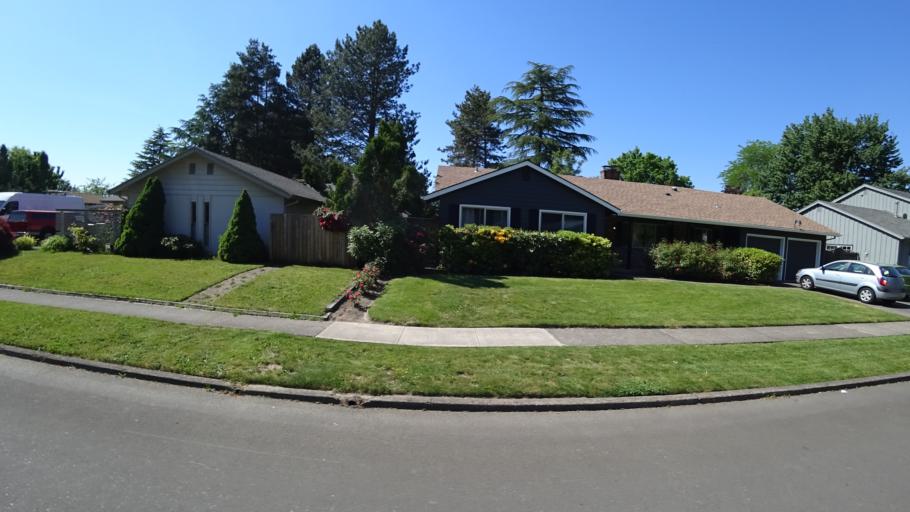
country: US
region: Oregon
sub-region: Washington County
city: Rockcreek
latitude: 45.5488
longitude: -122.8733
